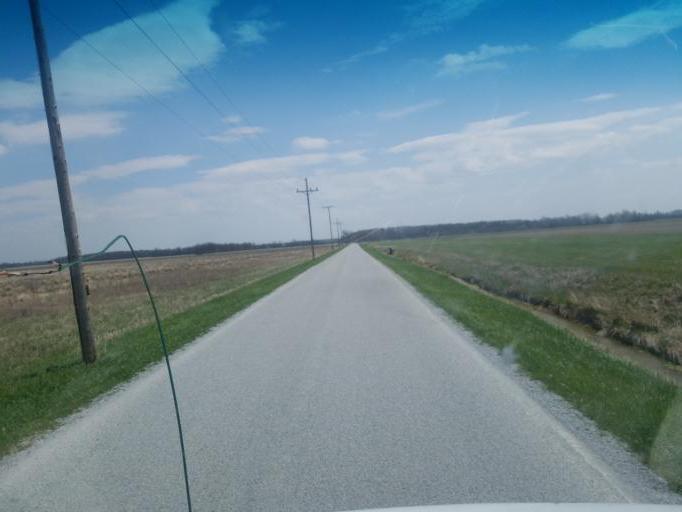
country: US
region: Ohio
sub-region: Hardin County
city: Forest
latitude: 40.7596
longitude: -83.5050
